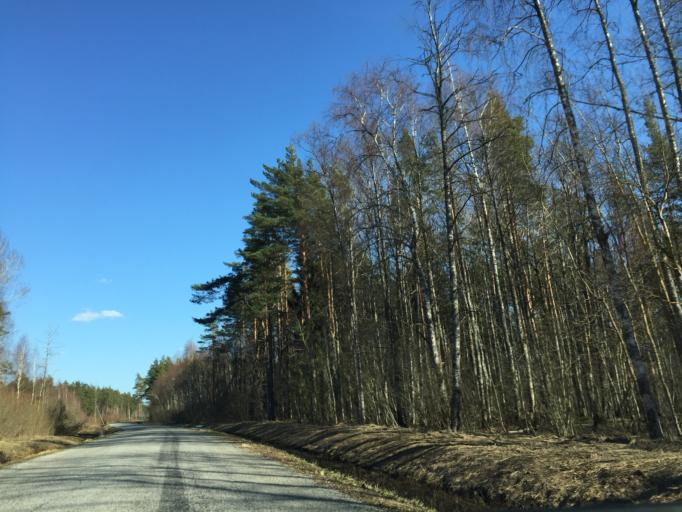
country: RU
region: Pskov
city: Gdov
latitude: 59.0099
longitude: 27.6443
